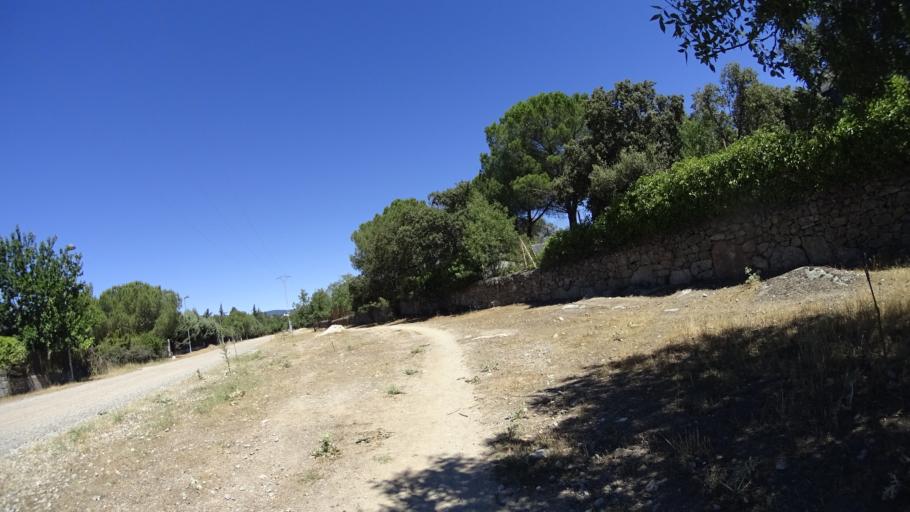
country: ES
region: Madrid
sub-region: Provincia de Madrid
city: Alpedrete
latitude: 40.6479
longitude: -4.0375
